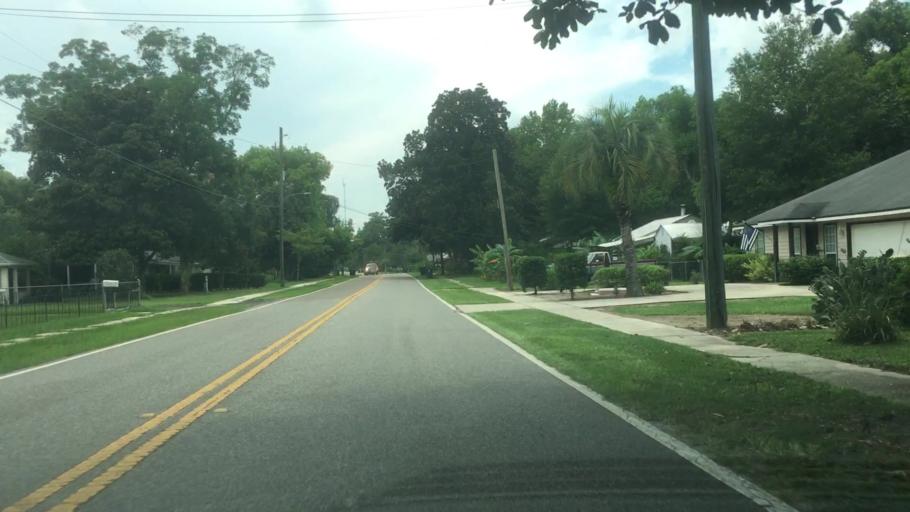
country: US
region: Florida
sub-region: Duval County
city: Jacksonville
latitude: 30.2996
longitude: -81.5497
